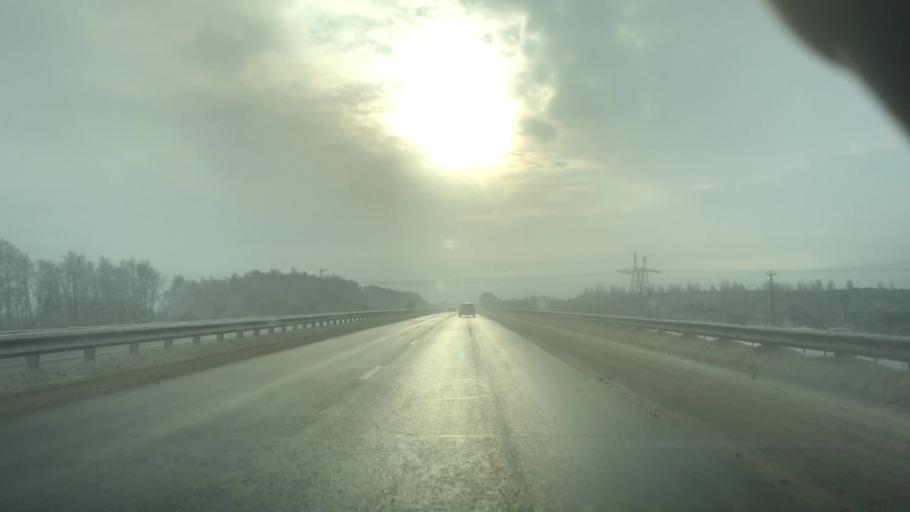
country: RU
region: Tula
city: Venev
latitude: 54.2944
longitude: 38.1576
